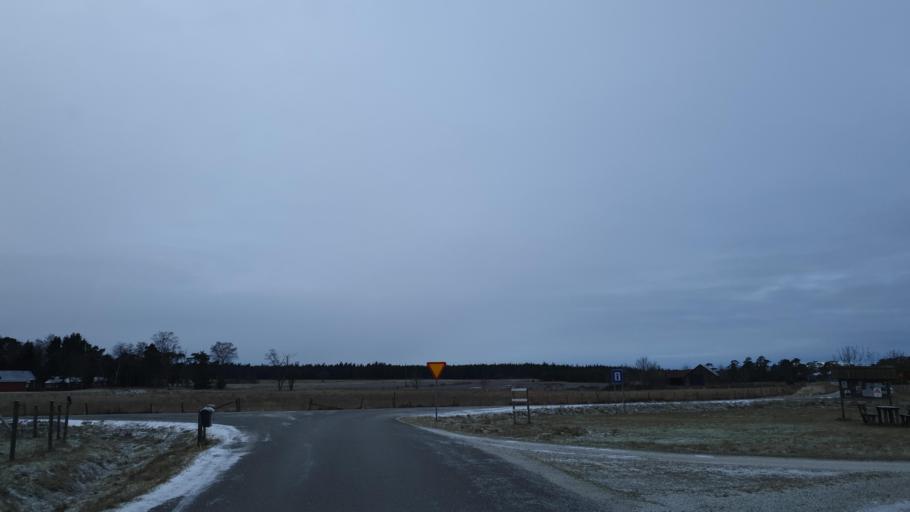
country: SE
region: Gotland
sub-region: Gotland
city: Slite
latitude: 57.3950
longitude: 18.8069
